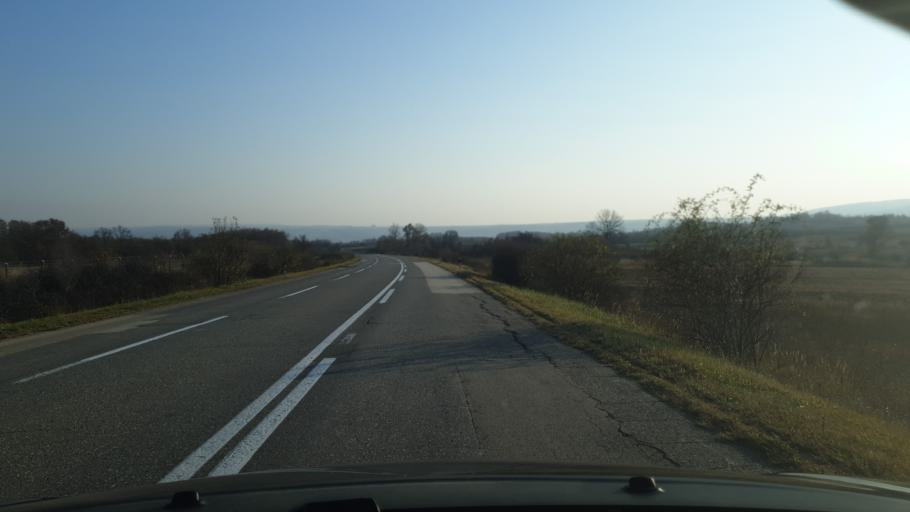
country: RS
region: Central Serbia
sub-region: Borski Okrug
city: Negotin
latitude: 44.1189
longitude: 22.3404
